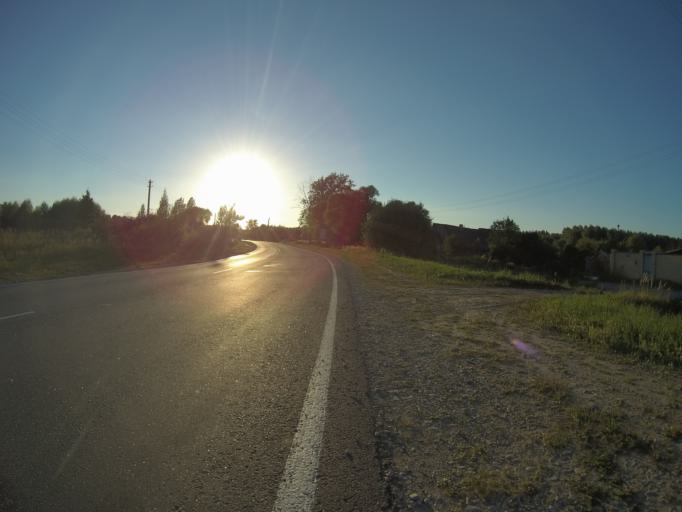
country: RU
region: Vladimir
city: Anopino
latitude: 55.7421
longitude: 40.7031
